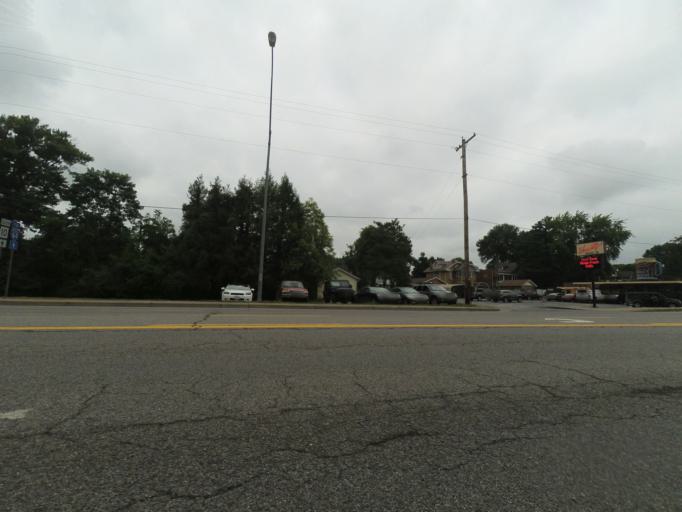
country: US
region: West Virginia
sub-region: Cabell County
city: Huntington
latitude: 38.4065
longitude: -82.4281
